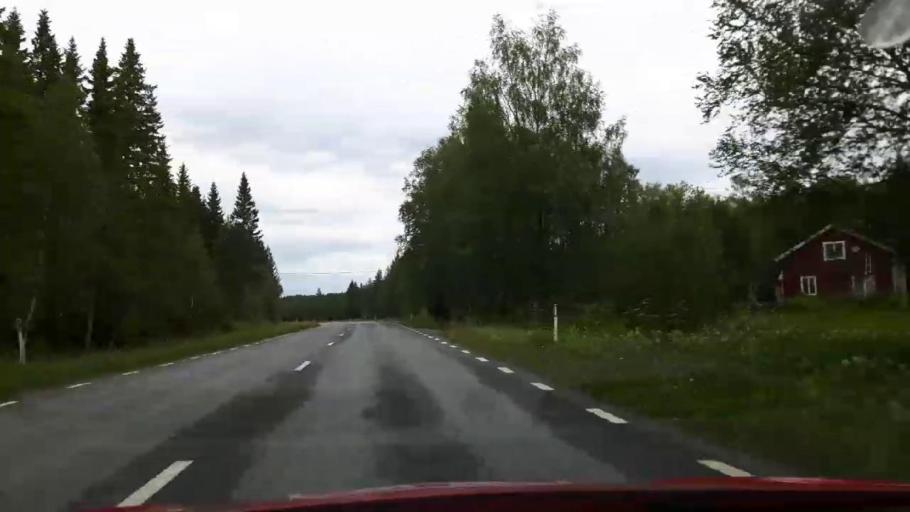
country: SE
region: Jaemtland
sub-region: Stroemsunds Kommun
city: Stroemsund
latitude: 63.5534
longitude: 15.3733
